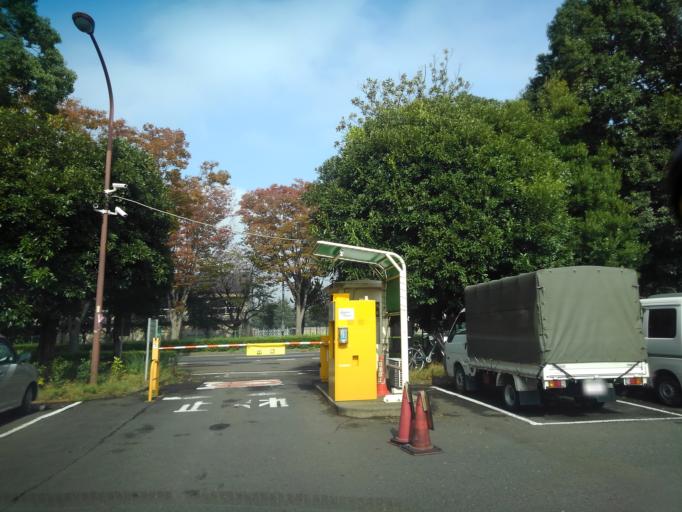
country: JP
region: Saitama
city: Tokorozawa
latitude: 35.8011
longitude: 139.4753
